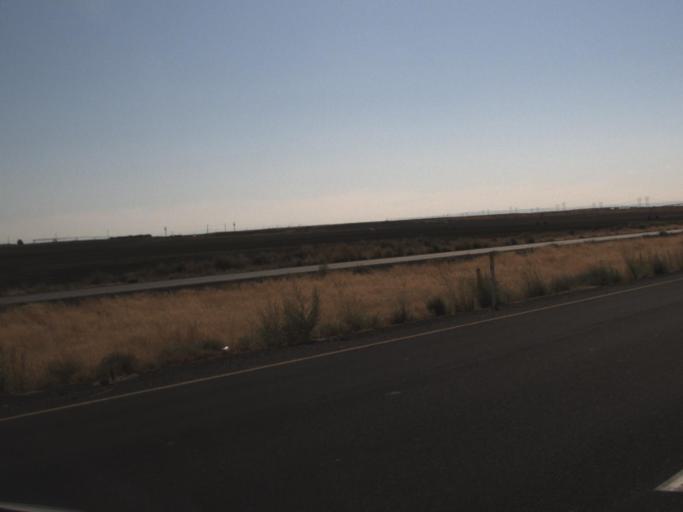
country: US
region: Washington
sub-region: Franklin County
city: Pasco
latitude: 46.3189
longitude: -119.0933
